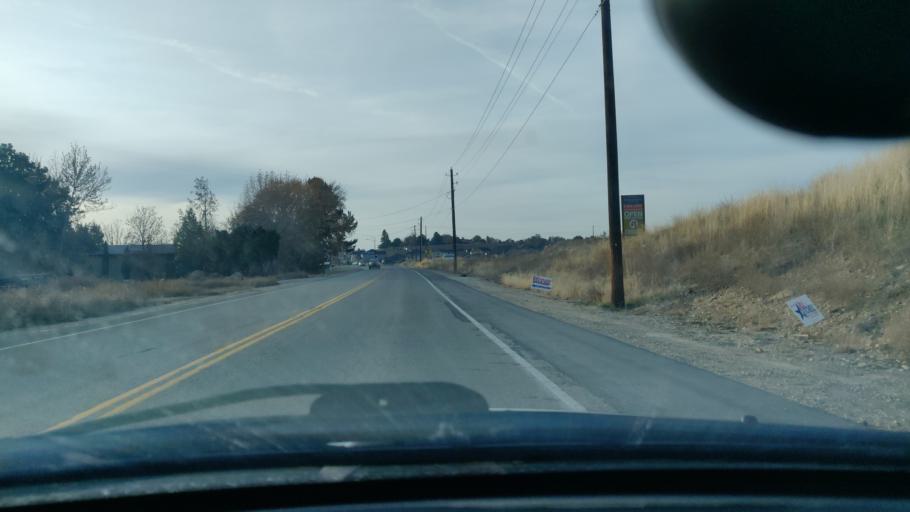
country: US
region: Idaho
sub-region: Ada County
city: Eagle
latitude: 43.6928
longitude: -116.3157
